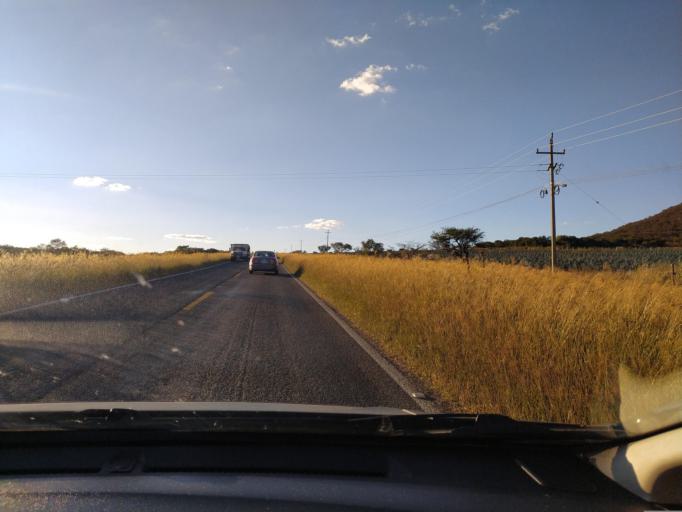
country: MX
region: Jalisco
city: San Julian
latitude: 21.0020
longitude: -102.1037
